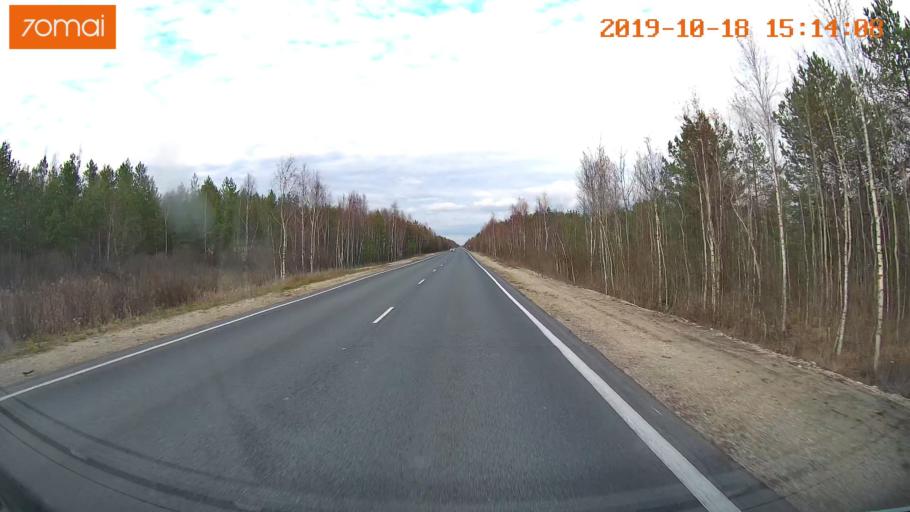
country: RU
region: Vladimir
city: Gus'-Khrustal'nyy
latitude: 55.5978
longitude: 40.7196
